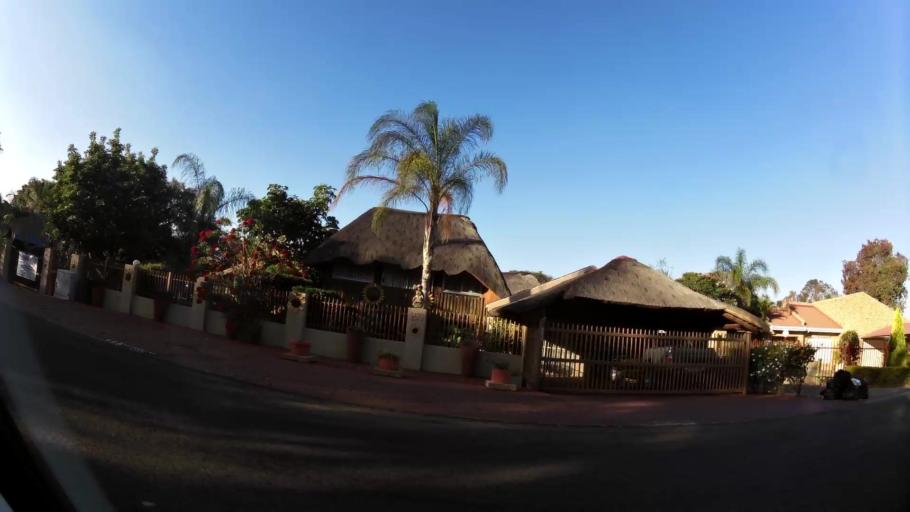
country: ZA
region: North-West
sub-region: Bojanala Platinum District Municipality
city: Rustenburg
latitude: -25.6807
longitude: 27.2026
